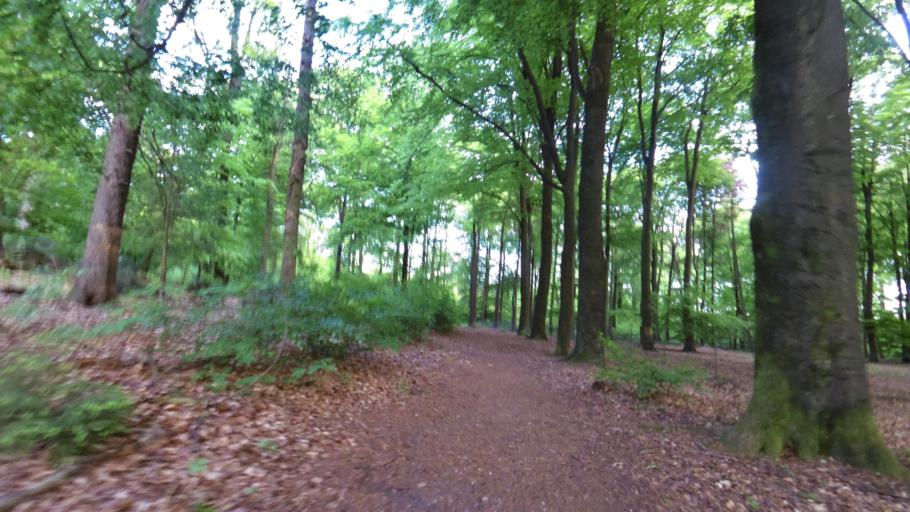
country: NL
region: Gelderland
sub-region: Gemeente Rozendaal
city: Rozendaal
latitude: 52.0119
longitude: 5.9642
